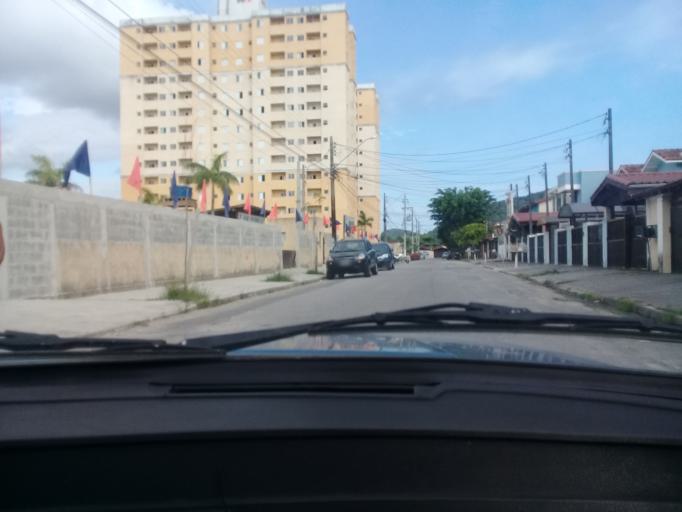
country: BR
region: Sao Paulo
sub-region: Guaruja
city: Guaruja
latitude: -23.9883
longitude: -46.2812
